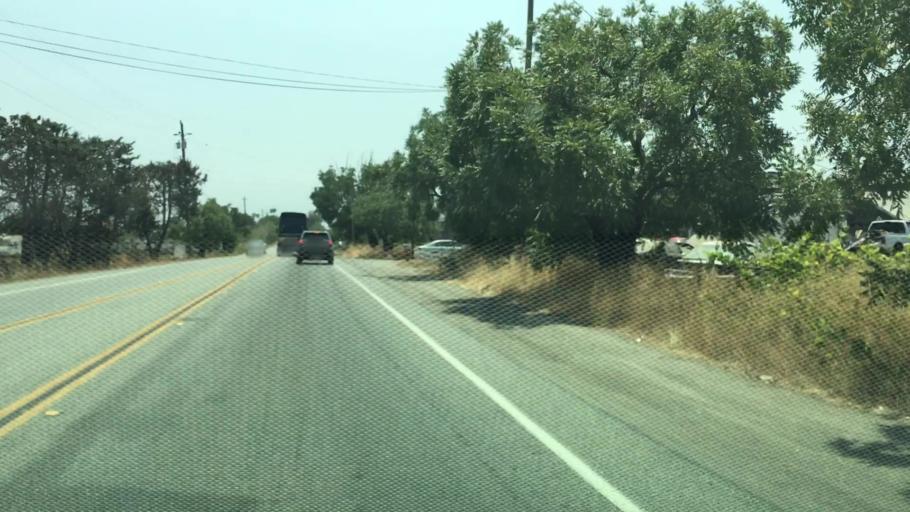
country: US
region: California
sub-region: Santa Clara County
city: Gilroy
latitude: 37.0175
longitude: -121.5205
